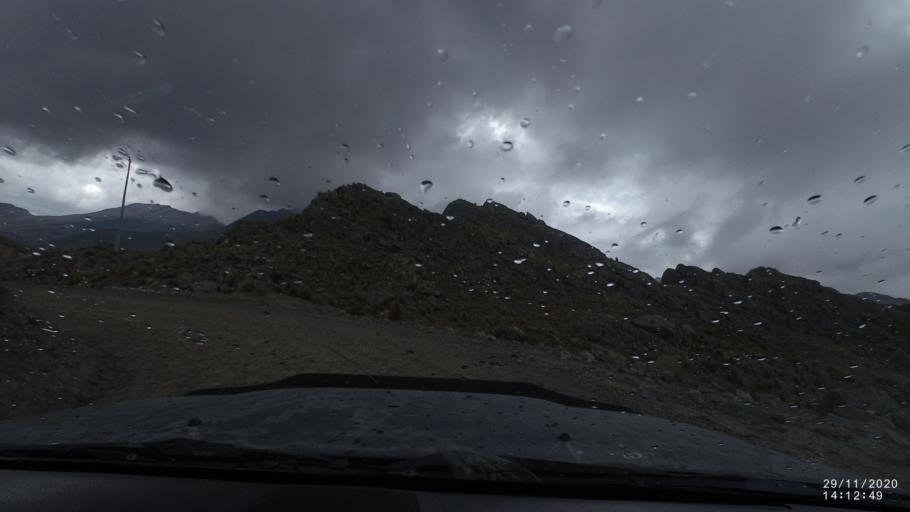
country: BO
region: Cochabamba
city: Sipe Sipe
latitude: -17.2405
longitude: -66.3948
